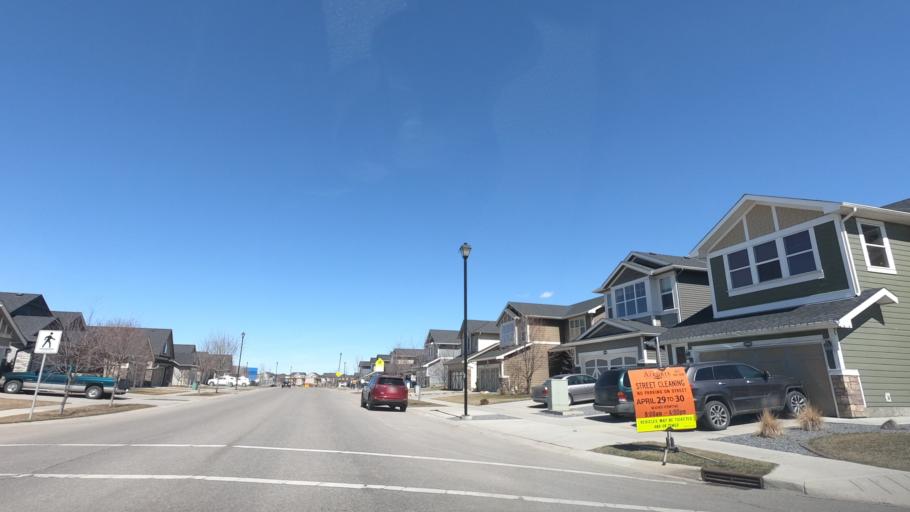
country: CA
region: Alberta
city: Airdrie
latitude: 51.3013
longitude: -114.0332
